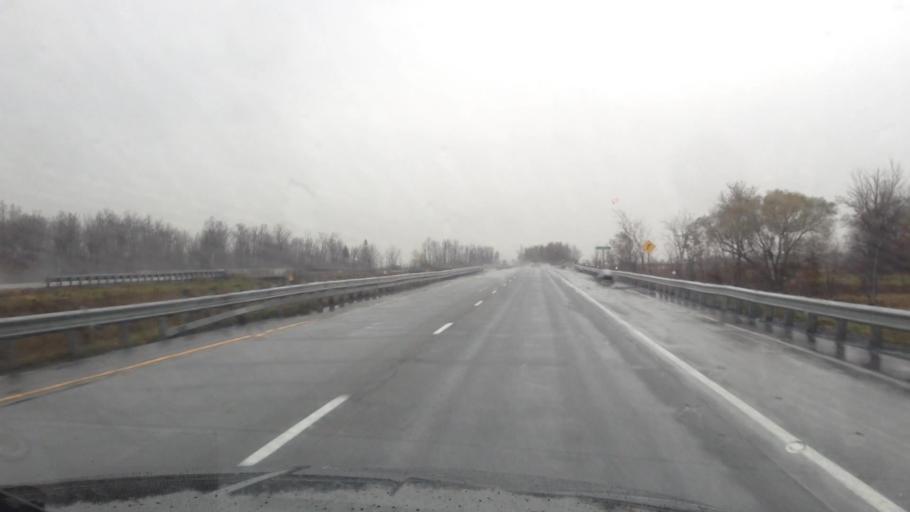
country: CA
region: Ontario
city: Casselman
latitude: 45.3527
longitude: -74.8883
